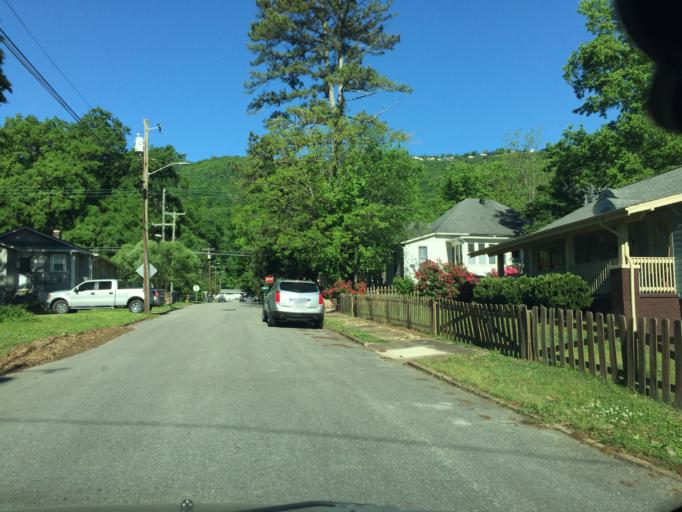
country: US
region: Tennessee
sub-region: Hamilton County
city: Lookout Mountain
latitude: 34.9925
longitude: -85.3302
